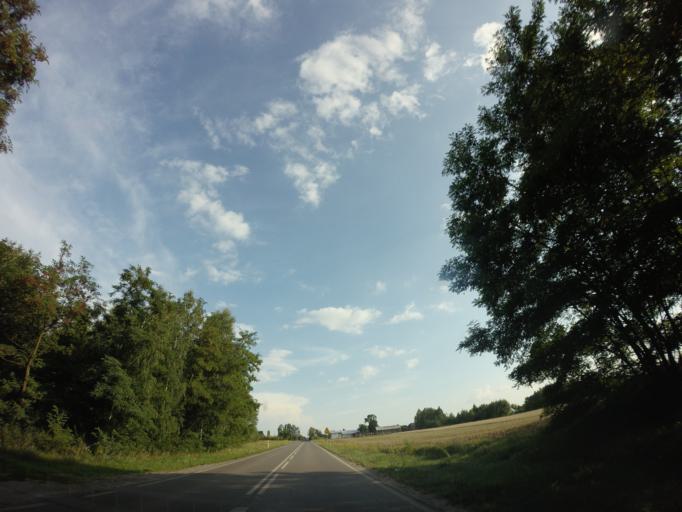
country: PL
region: Lublin Voivodeship
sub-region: Powiat lubartowski
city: Michow
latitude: 51.5544
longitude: 22.2989
